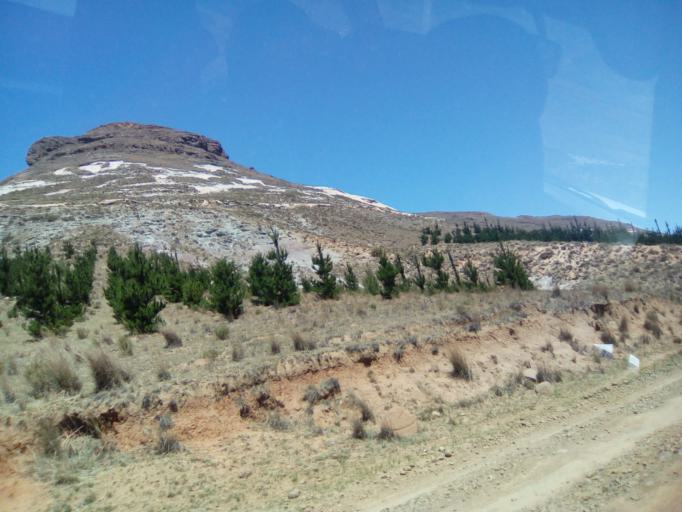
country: LS
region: Qacha's Nek
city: Qacha's Nek
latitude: -30.0375
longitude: 28.6806
